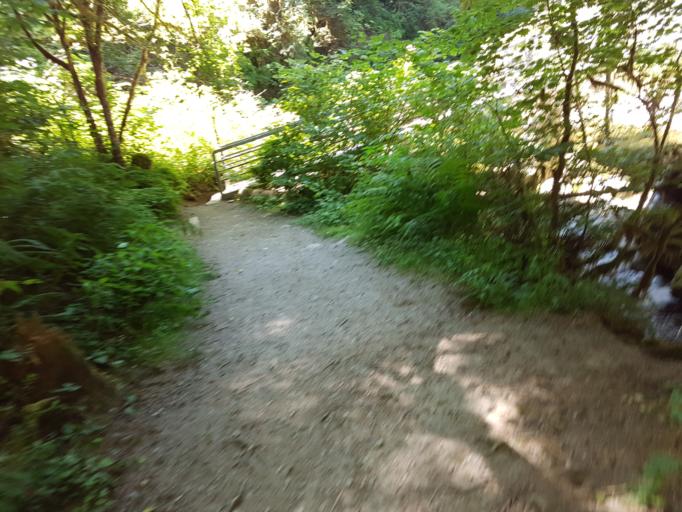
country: CA
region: British Columbia
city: Maple Ridge
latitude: 49.2114
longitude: -122.5178
